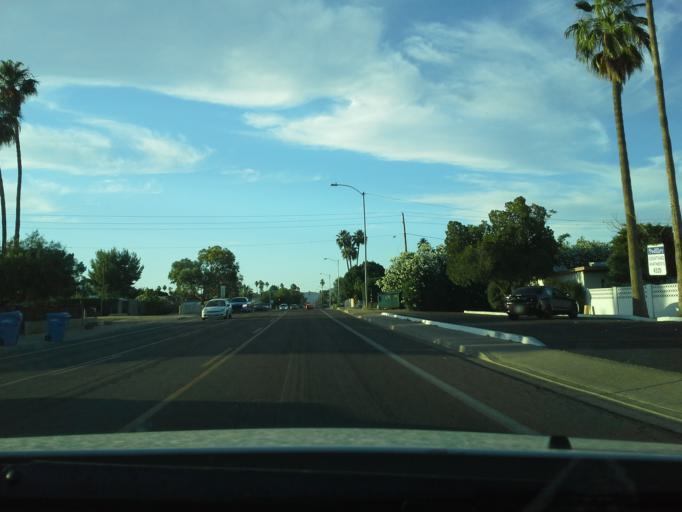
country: US
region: Arizona
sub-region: Maricopa County
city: Phoenix
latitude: 33.4998
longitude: -112.0913
